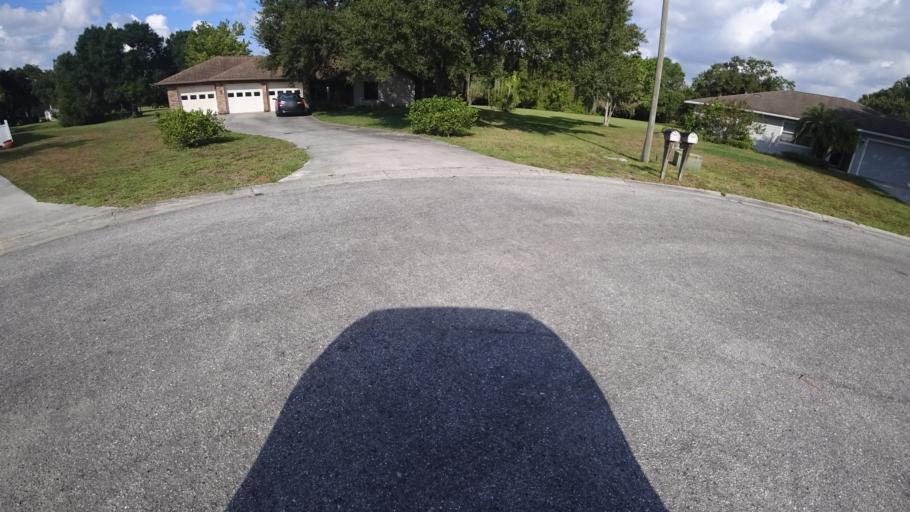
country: US
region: Florida
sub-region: Sarasota County
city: Desoto Lakes
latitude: 27.4319
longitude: -82.4532
